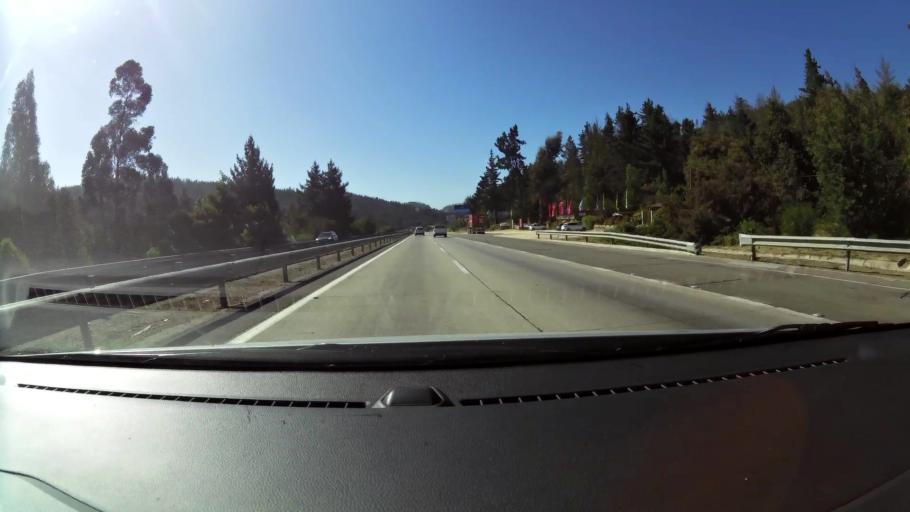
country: CL
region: Valparaiso
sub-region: Provincia de Marga Marga
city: Quilpue
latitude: -33.2313
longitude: -71.4644
